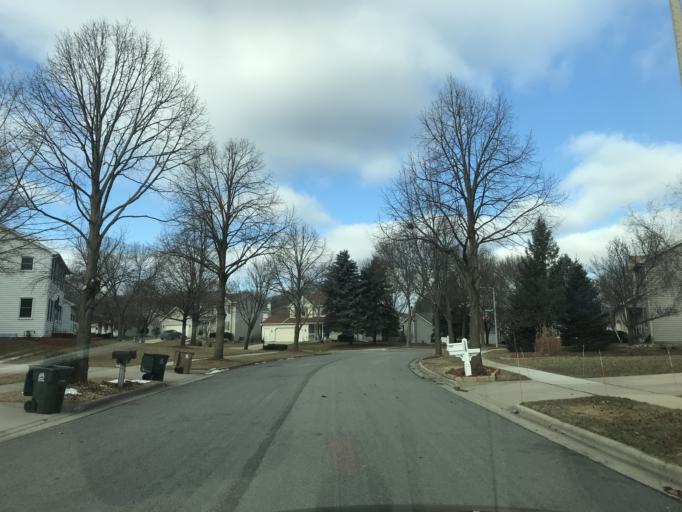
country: US
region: Wisconsin
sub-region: Dane County
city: Monona
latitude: 43.1150
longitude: -89.2977
